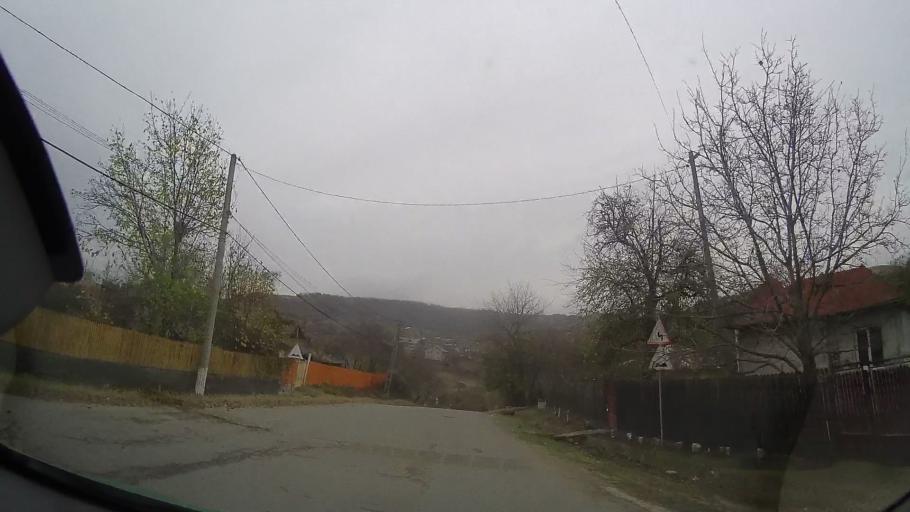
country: RO
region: Prahova
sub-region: Comuna Gornet-Cricov
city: Gornet-Cricov
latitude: 45.0547
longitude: 26.2938
